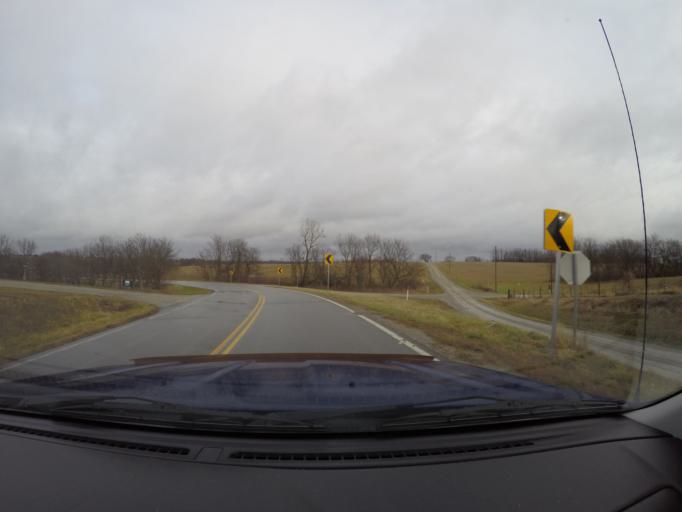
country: US
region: Kansas
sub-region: Jefferson County
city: Oskaloosa
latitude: 39.3320
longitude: -95.1434
